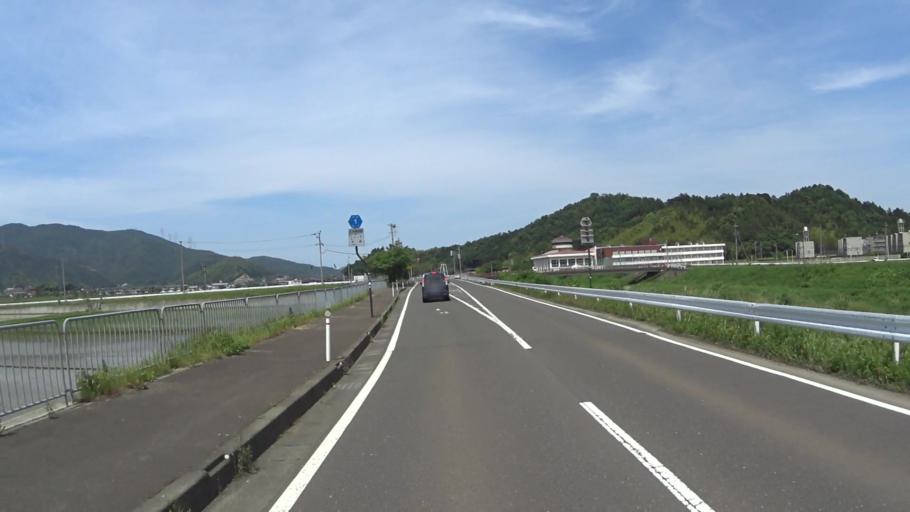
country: JP
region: Fukui
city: Obama
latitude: 35.4701
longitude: 135.6201
